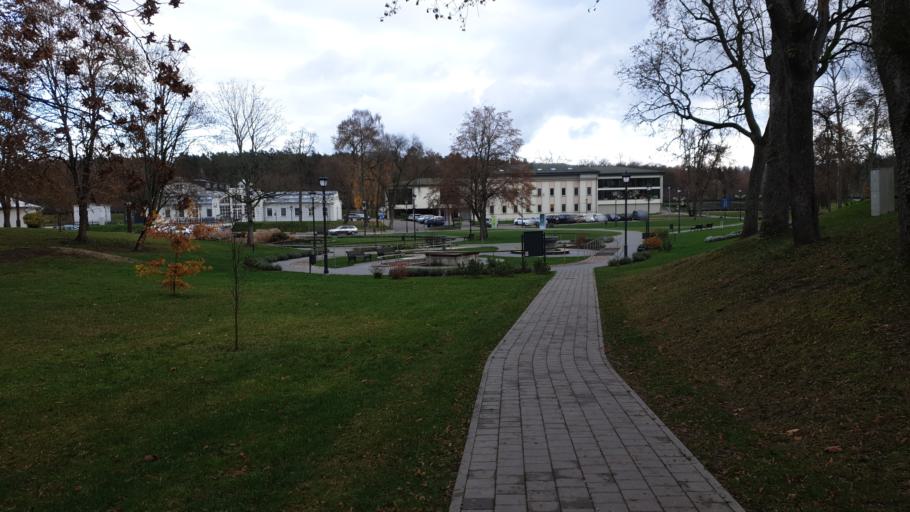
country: LT
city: Birstonas
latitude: 54.6010
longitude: 24.0331
